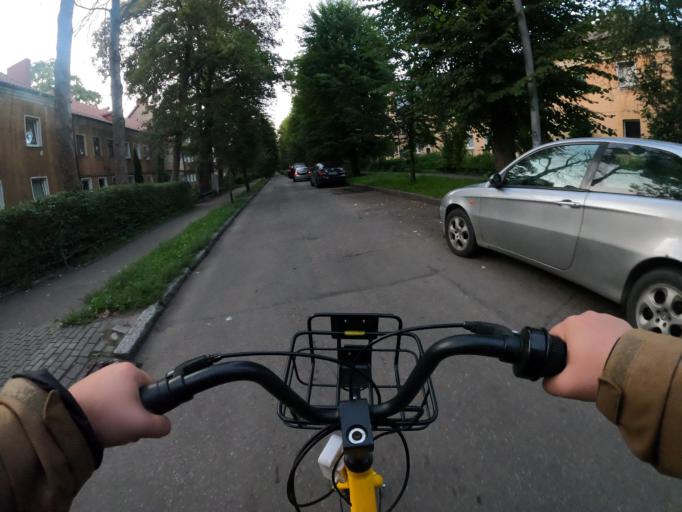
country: RU
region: Kaliningrad
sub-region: Gorod Kaliningrad
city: Kaliningrad
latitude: 54.7236
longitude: 20.4768
